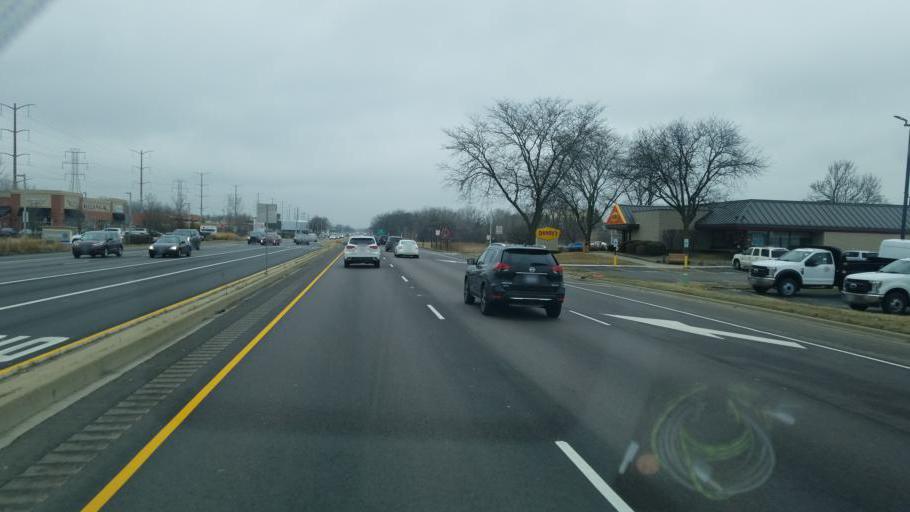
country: US
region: Illinois
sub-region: Lake County
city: Highwood
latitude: 42.1891
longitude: -87.8262
